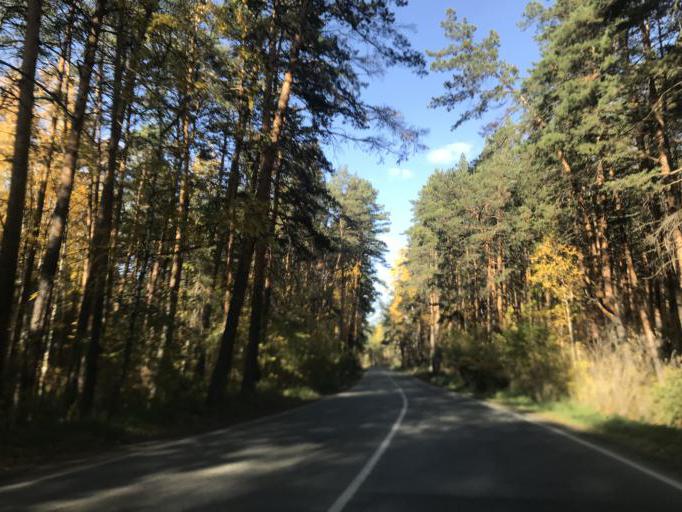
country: RU
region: Chelyabinsk
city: Dolgoderevenskoye
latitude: 55.2937
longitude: 61.3581
